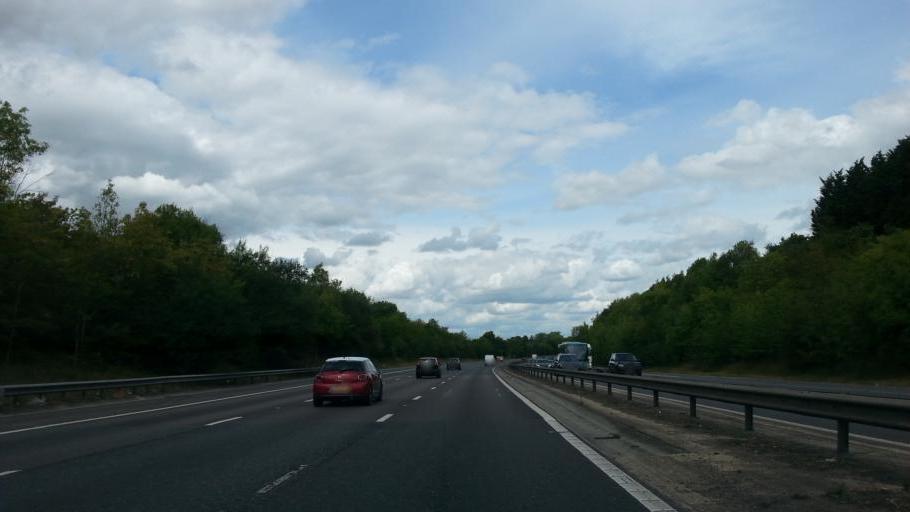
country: GB
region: England
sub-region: Hertfordshire
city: Sawbridgeworth
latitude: 51.8036
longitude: 0.1760
